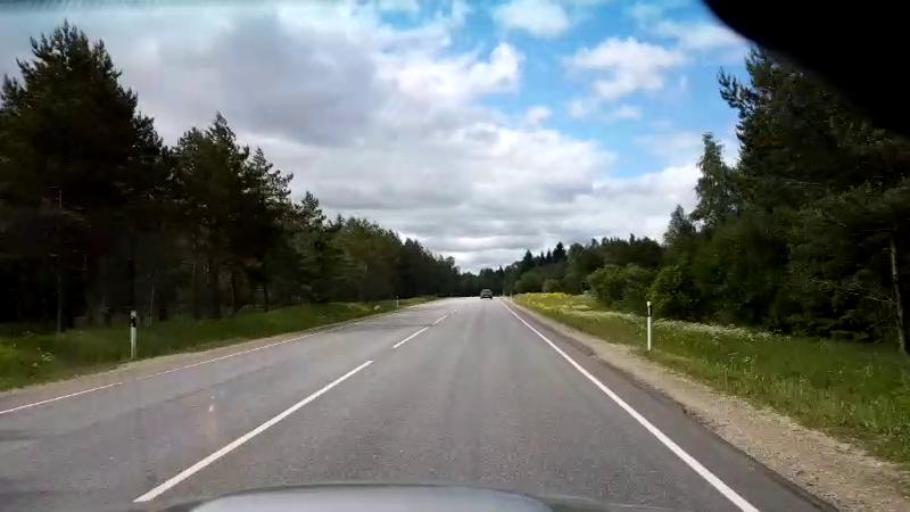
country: EE
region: Raplamaa
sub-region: Maerjamaa vald
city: Marjamaa
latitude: 58.9531
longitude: 24.4694
